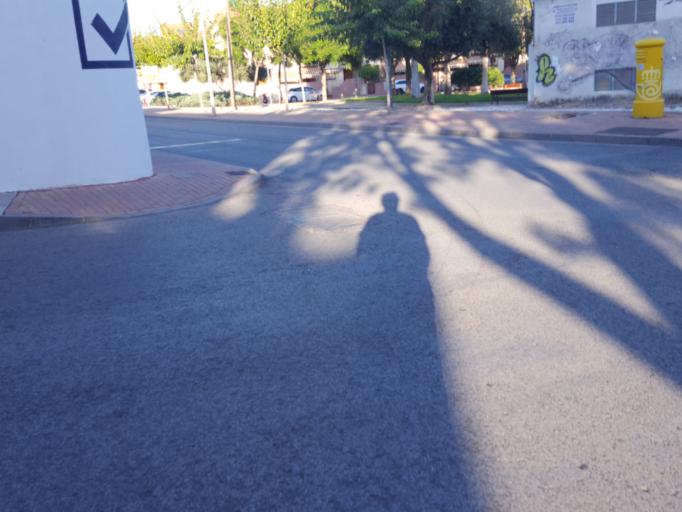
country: ES
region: Murcia
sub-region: Murcia
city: Murcia
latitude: 37.9979
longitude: -1.1741
